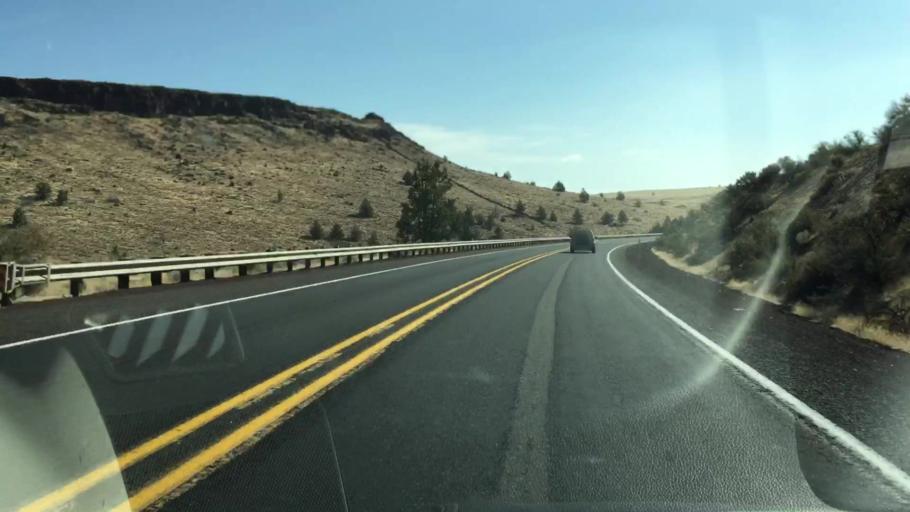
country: US
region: Oregon
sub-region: Jefferson County
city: Madras
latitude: 44.7666
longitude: -121.0106
